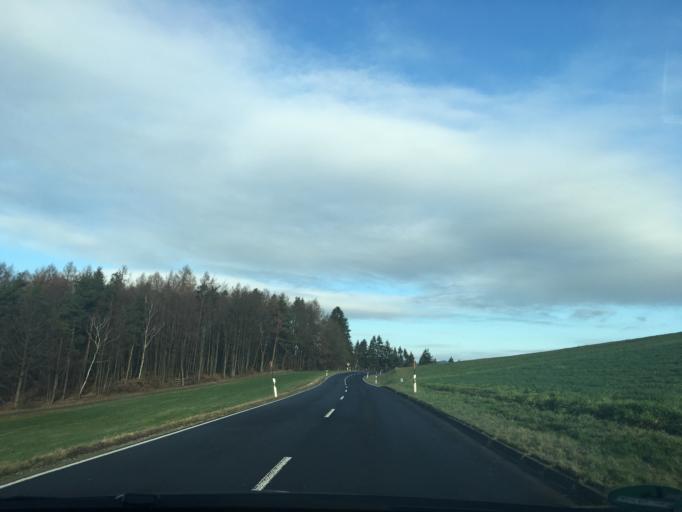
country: DE
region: Hesse
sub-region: Regierungsbezirk Kassel
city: Hofbieber
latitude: 50.5994
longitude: 9.8755
